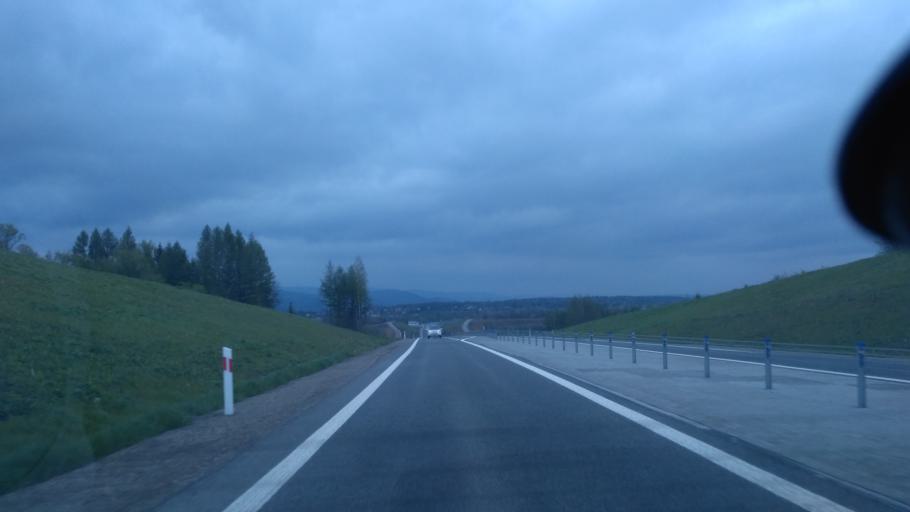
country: PL
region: Subcarpathian Voivodeship
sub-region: Powiat sanocki
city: Sanok
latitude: 49.5414
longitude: 22.1951
